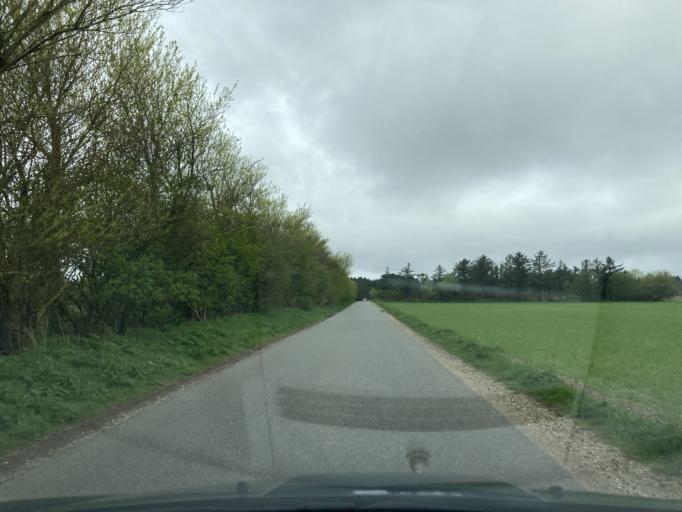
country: DK
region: North Denmark
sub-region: Thisted Kommune
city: Hurup
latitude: 56.8142
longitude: 8.3267
